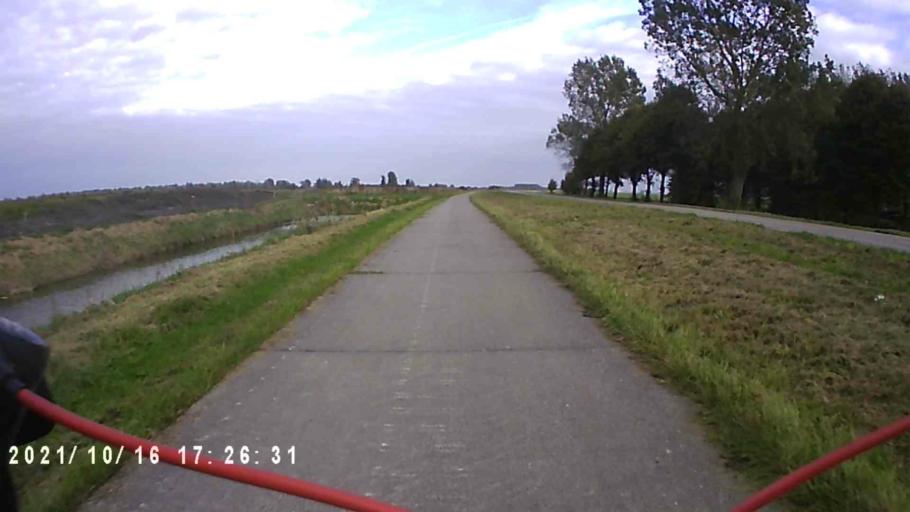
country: NL
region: Friesland
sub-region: Gemeente Kollumerland en Nieuwkruisland
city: Kollum
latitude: 53.3208
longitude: 6.1947
